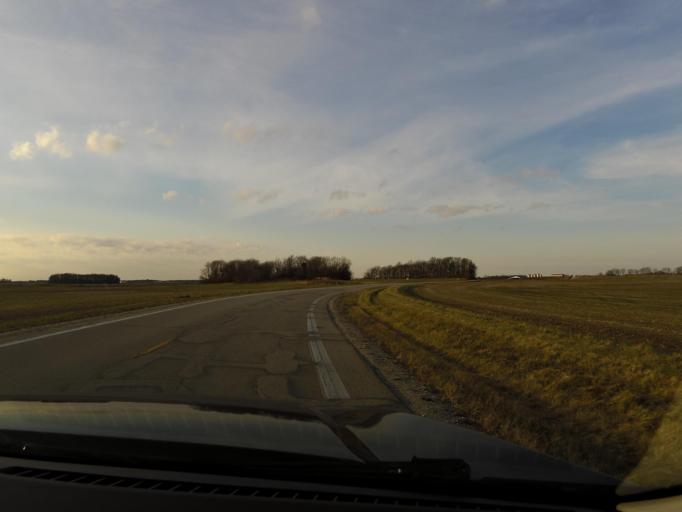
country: US
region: Illinois
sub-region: Fayette County
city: Vandalia
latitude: 38.9537
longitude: -89.1332
